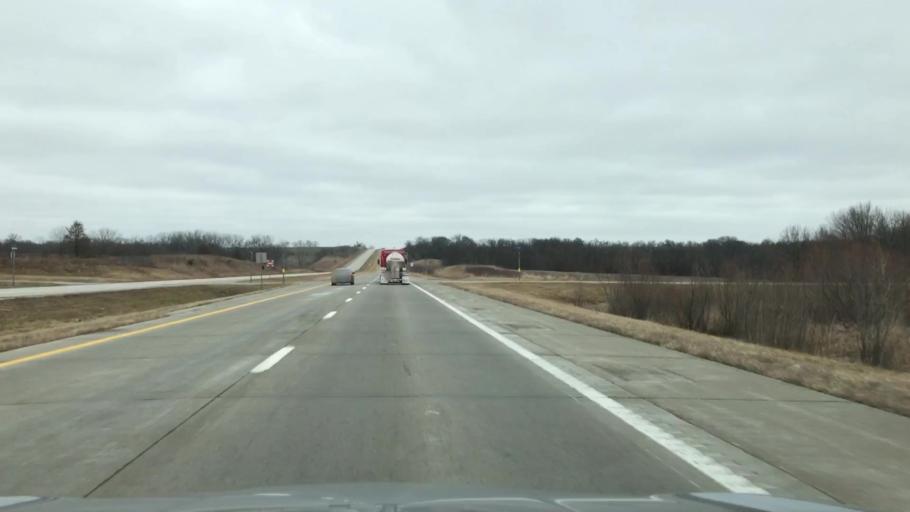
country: US
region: Missouri
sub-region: Caldwell County
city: Hamilton
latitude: 39.7349
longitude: -93.9462
